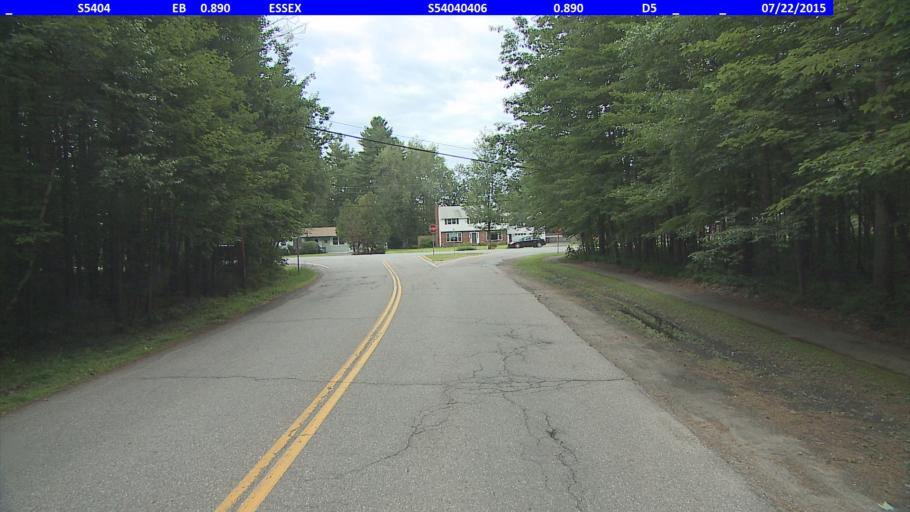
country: US
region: Vermont
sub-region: Chittenden County
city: Jericho
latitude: 44.5040
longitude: -73.0388
